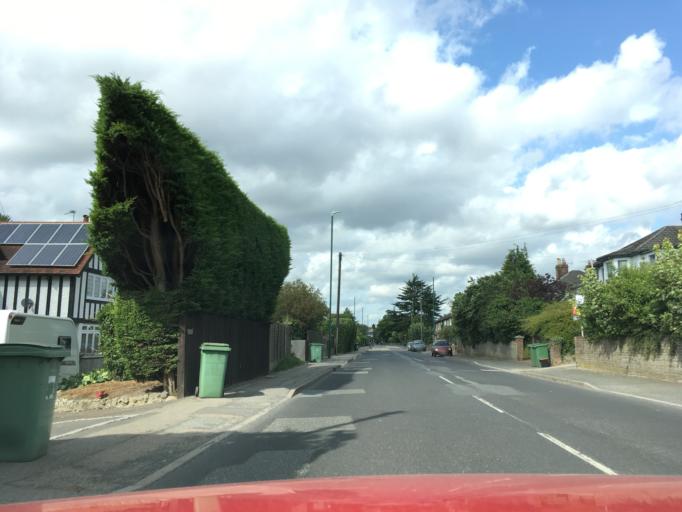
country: GB
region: England
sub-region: Kent
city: Maidstone
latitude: 51.2450
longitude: 0.5235
